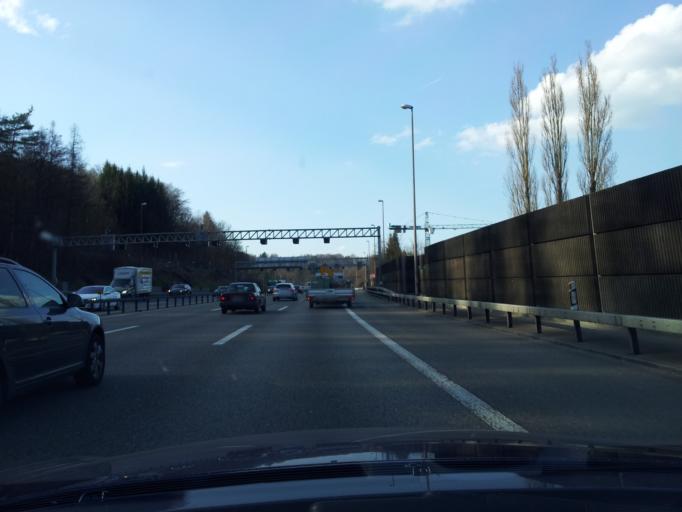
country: CH
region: Aargau
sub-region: Bezirk Baden
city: Neuenhof
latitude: 47.4550
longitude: 8.3087
